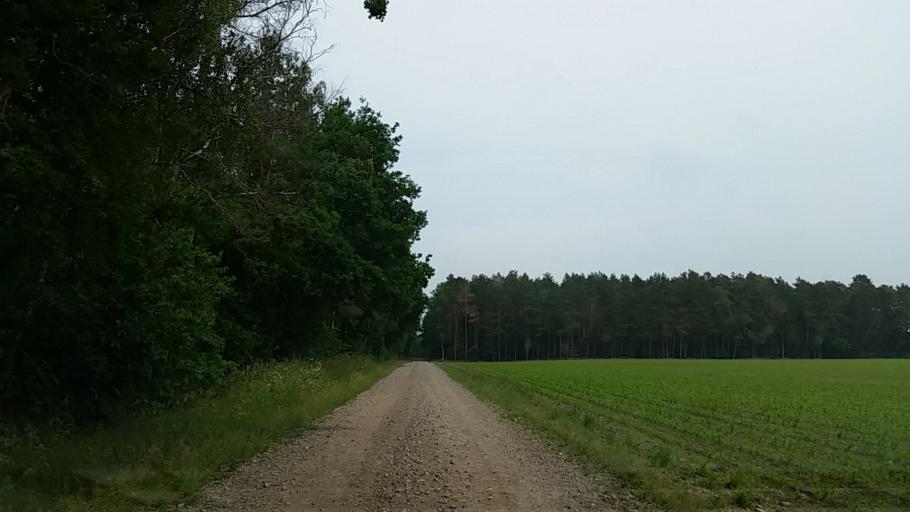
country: DE
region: Lower Saxony
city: Dedelstorf
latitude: 52.6885
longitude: 10.5295
